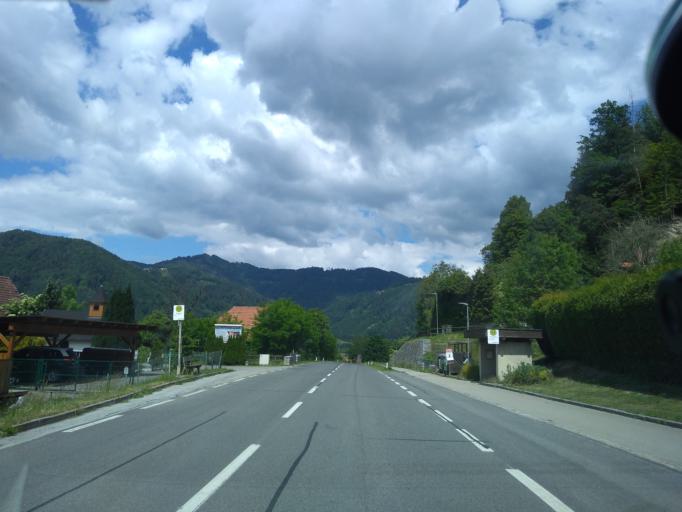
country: AT
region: Styria
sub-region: Politischer Bezirk Graz-Umgebung
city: Frohnleiten
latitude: 47.2396
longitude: 15.3269
